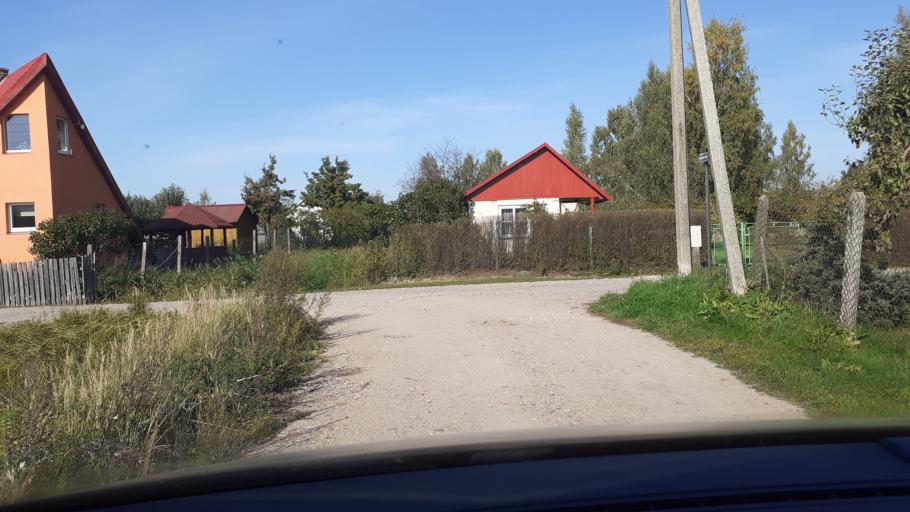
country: LV
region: Kuldigas Rajons
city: Kuldiga
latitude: 56.9502
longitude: 21.9778
